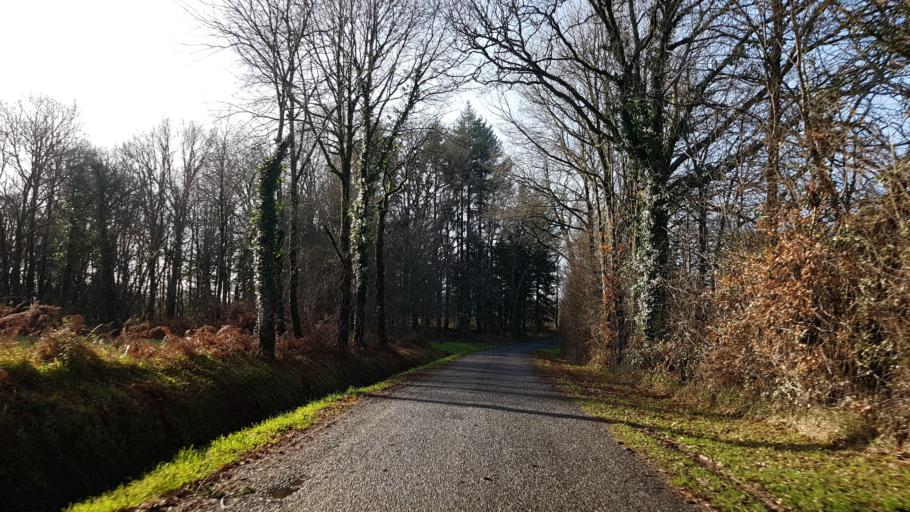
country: FR
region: Poitou-Charentes
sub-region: Departement de la Charente
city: Etagnac
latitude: 45.9132
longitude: 0.8202
